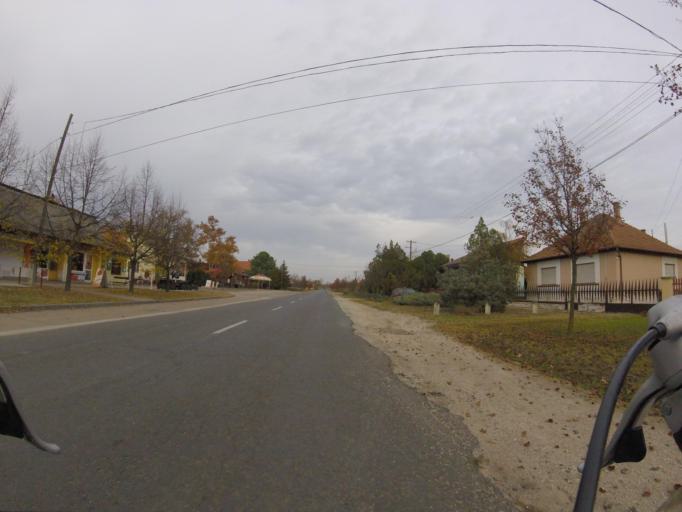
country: HU
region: Pest
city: Csemo
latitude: 47.1156
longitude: 19.6959
